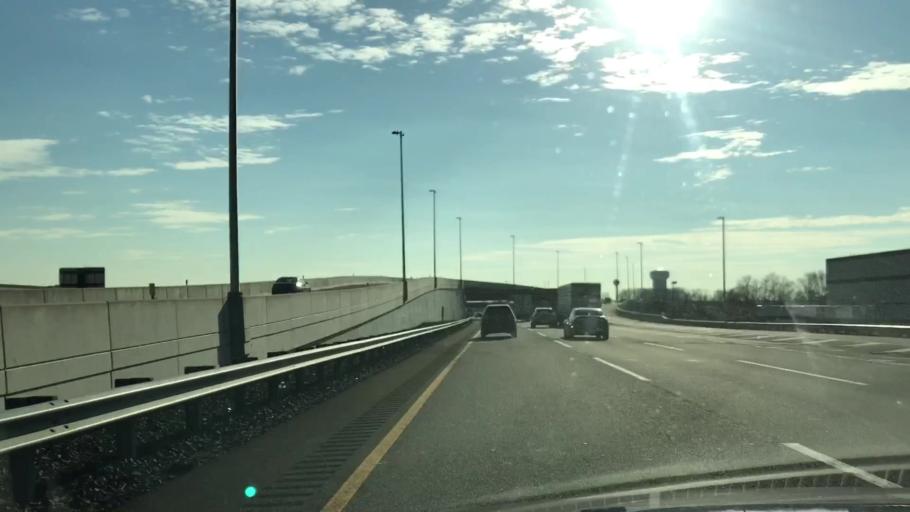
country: US
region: New Jersey
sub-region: Middlesex County
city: Rossmoor
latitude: 40.3310
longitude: -74.4817
